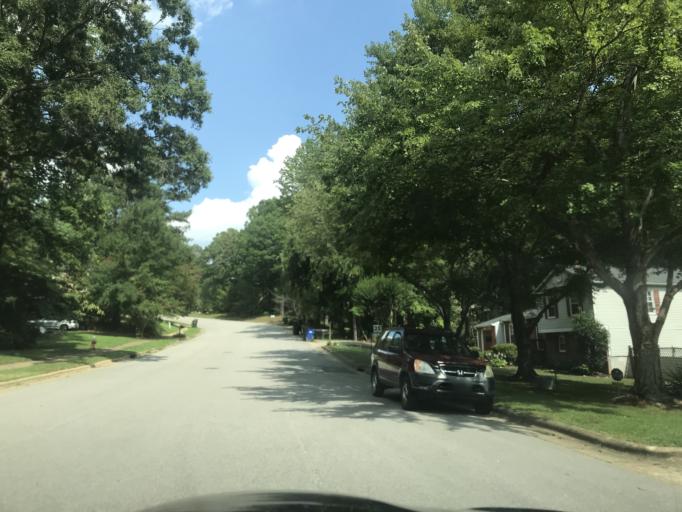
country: US
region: North Carolina
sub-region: Wake County
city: West Raleigh
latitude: 35.8761
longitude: -78.6585
